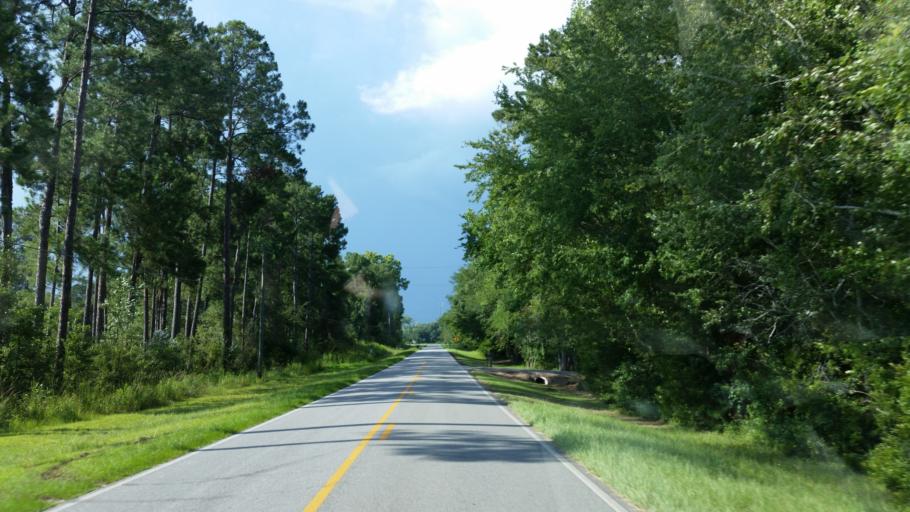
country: US
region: Georgia
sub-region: Lowndes County
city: Hahira
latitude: 30.9805
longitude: -83.3955
